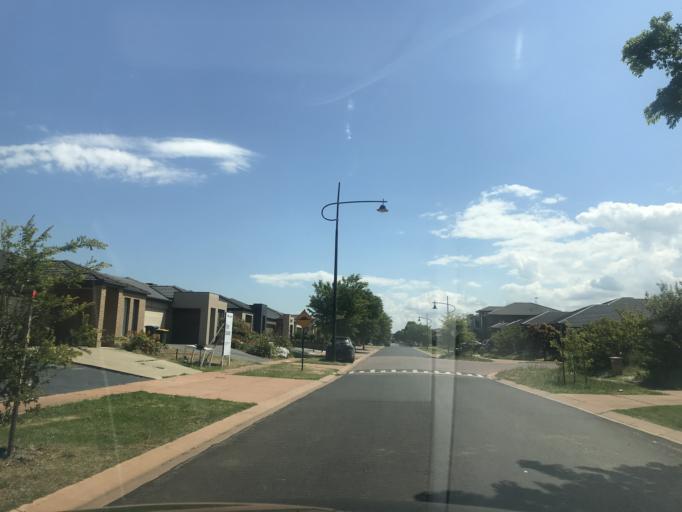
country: AU
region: Victoria
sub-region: Wyndham
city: Hoppers Crossing
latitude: -37.8891
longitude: 144.7248
